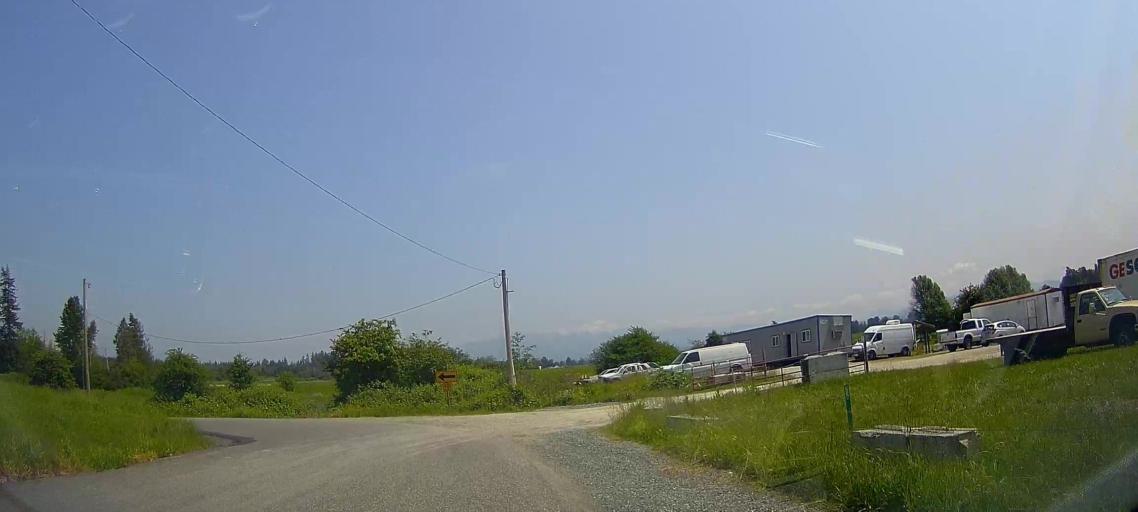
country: US
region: Washington
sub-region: Skagit County
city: Mount Vernon
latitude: 48.4577
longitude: -122.4129
